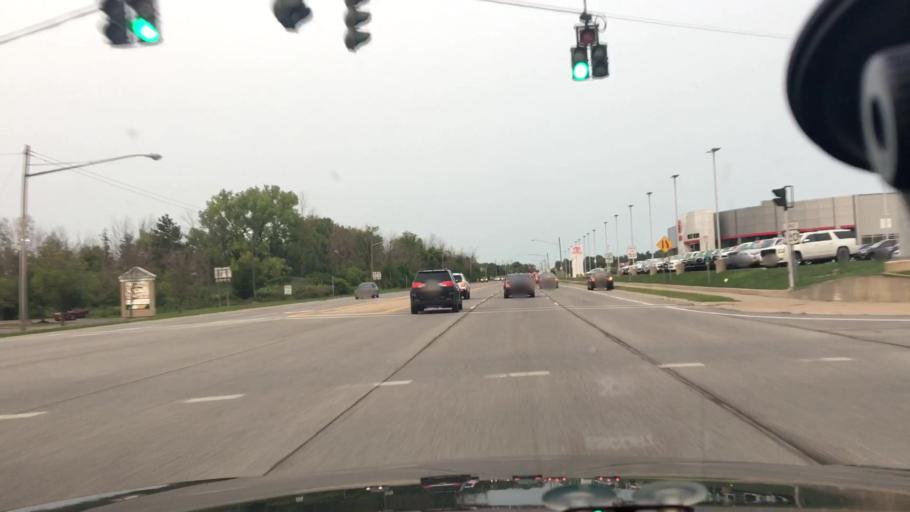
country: US
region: New York
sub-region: Erie County
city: Blasdell
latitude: 42.7707
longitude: -78.8097
